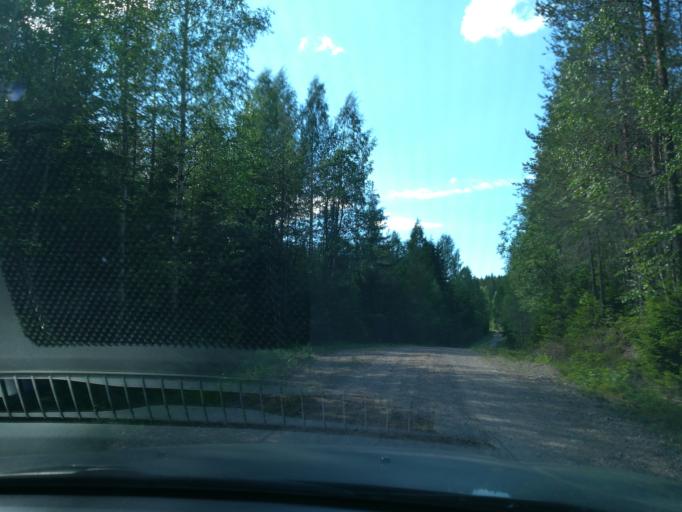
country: FI
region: South Karelia
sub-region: Imatra
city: Ruokolahti
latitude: 61.5431
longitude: 28.8084
